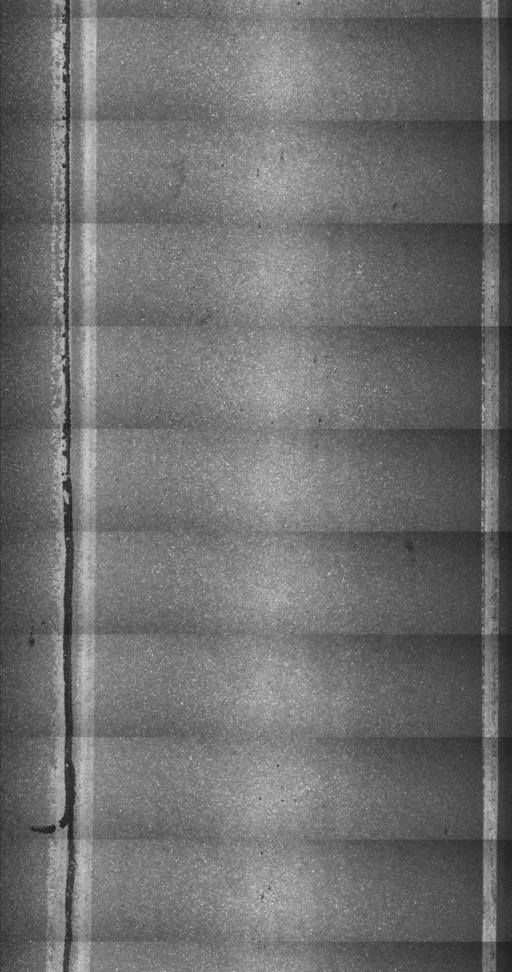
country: US
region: Vermont
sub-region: Chittenden County
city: Milton
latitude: 44.6250
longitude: -73.0198
